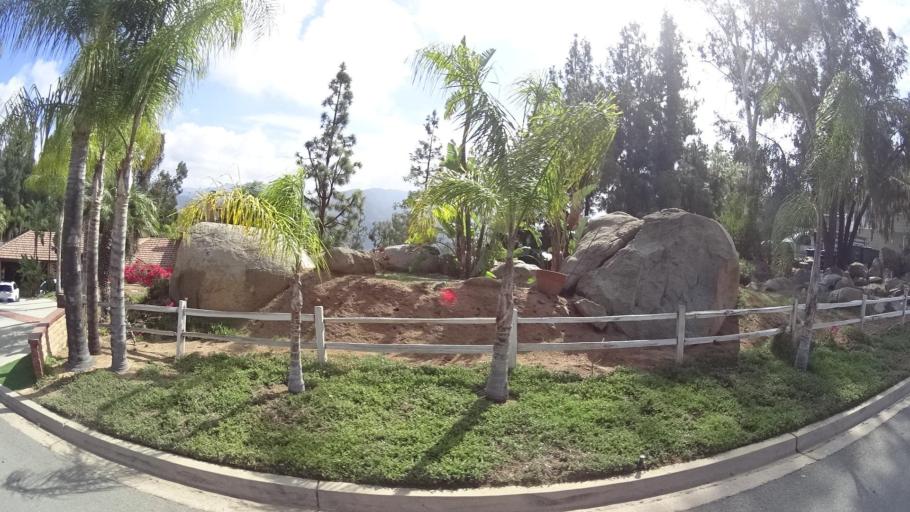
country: US
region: California
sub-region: San Diego County
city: Granite Hills
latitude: 32.7779
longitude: -116.8962
